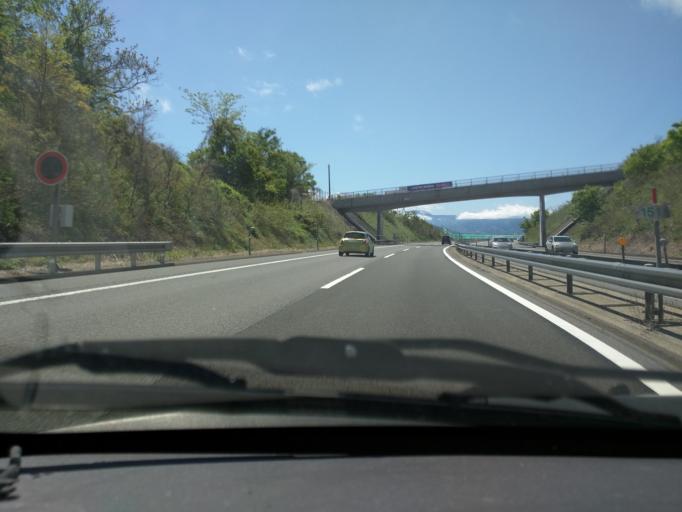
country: JP
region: Nagano
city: Nakano
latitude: 36.7753
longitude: 138.3188
